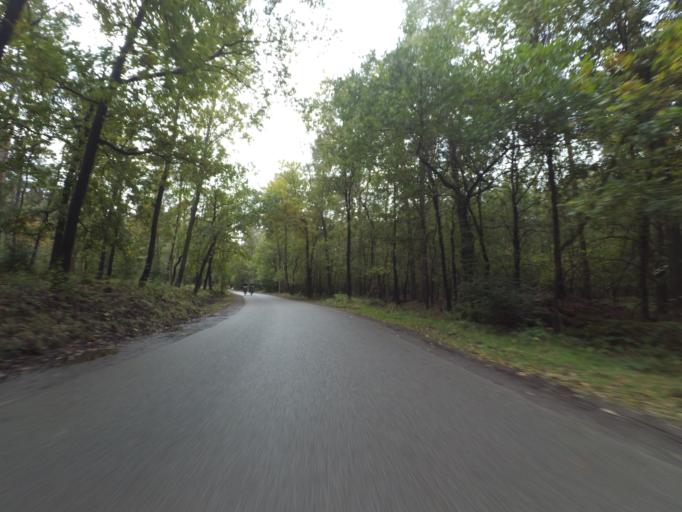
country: NL
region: Gelderland
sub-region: Gemeente Apeldoorn
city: Uddel
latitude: 52.3104
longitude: 5.7392
